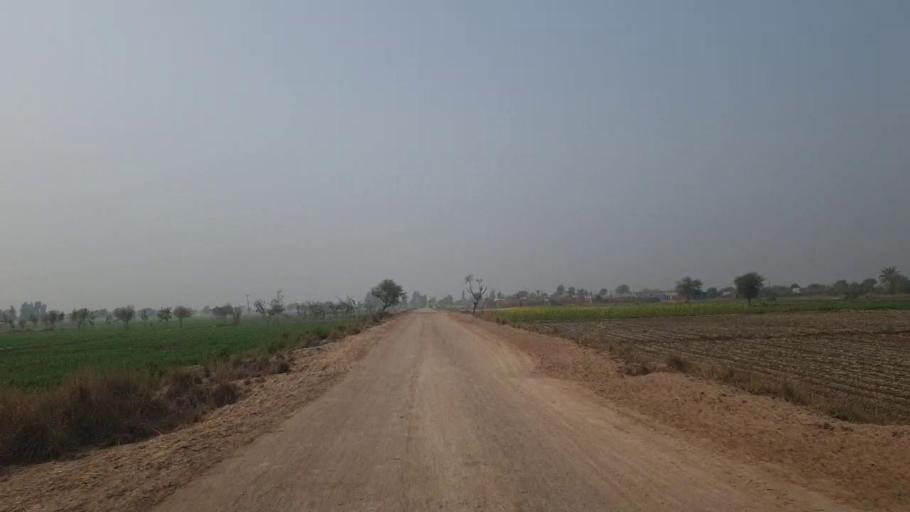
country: PK
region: Sindh
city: Shahdadpur
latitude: 25.8388
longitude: 68.5807
